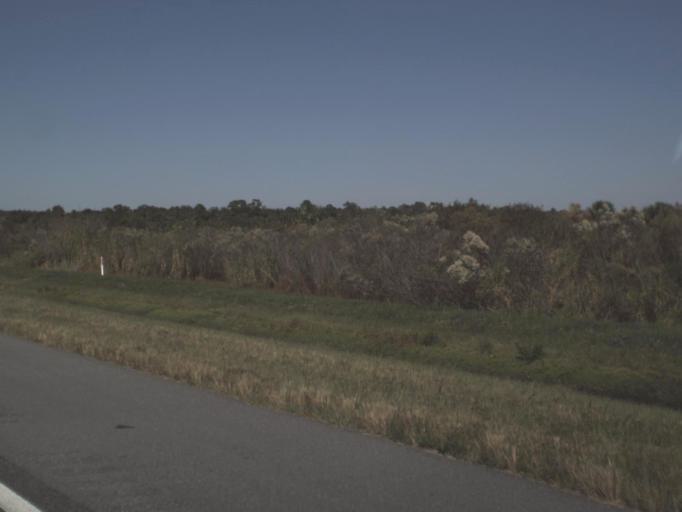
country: US
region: Florida
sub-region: Seminole County
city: Midway
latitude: 28.7302
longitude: -81.2493
